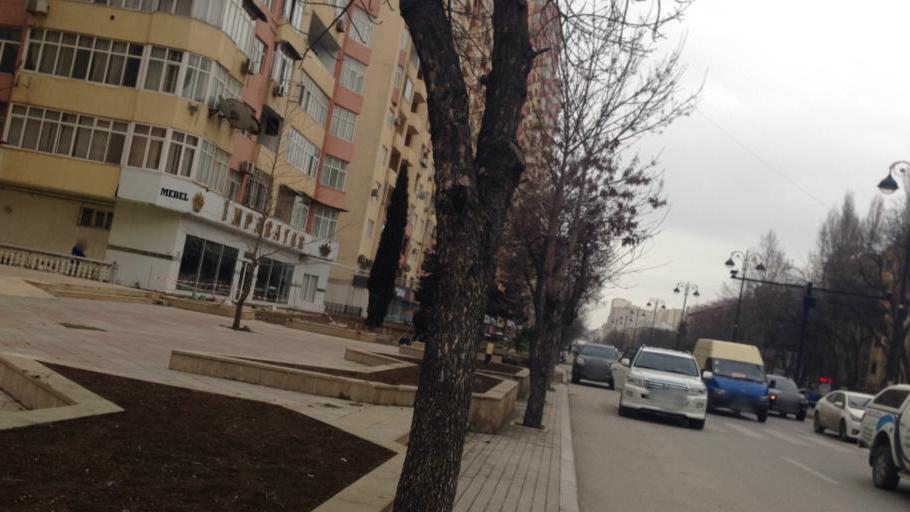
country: AZ
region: Baki
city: Khodzhi-Gasan
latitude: 40.3882
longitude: 49.8078
